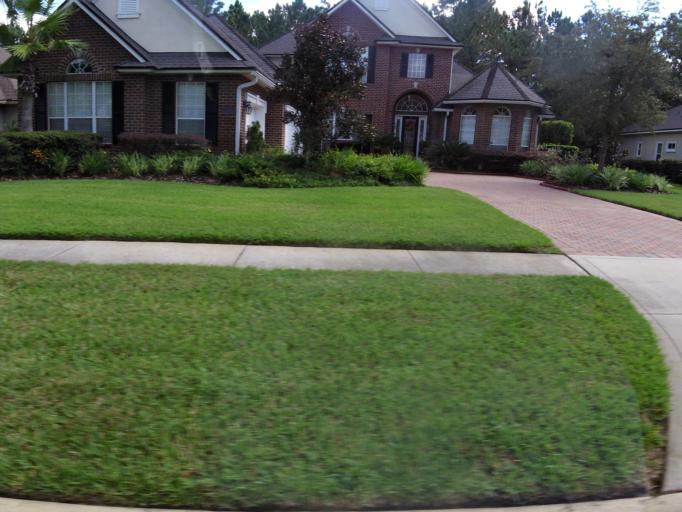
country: US
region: Florida
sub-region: Saint Johns County
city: Fruit Cove
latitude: 30.0617
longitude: -81.6420
